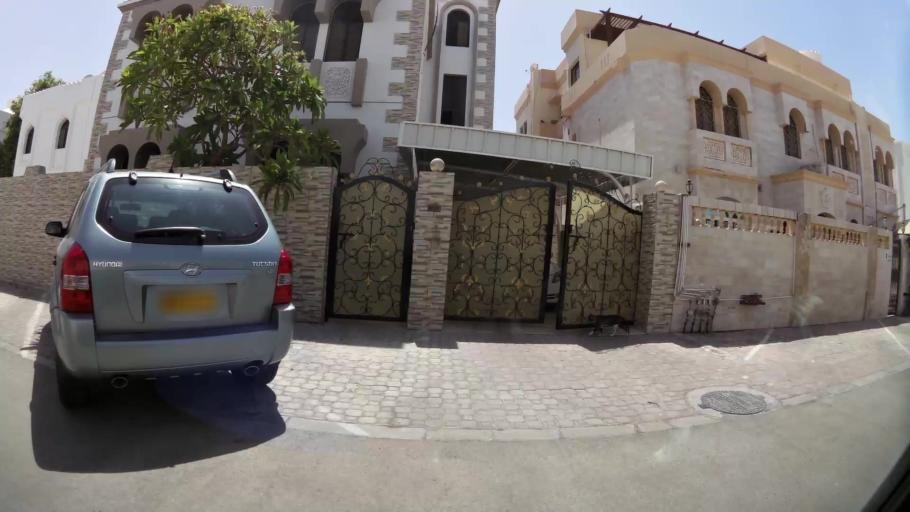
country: OM
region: Muhafazat Masqat
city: Muscat
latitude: 23.6147
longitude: 58.4997
